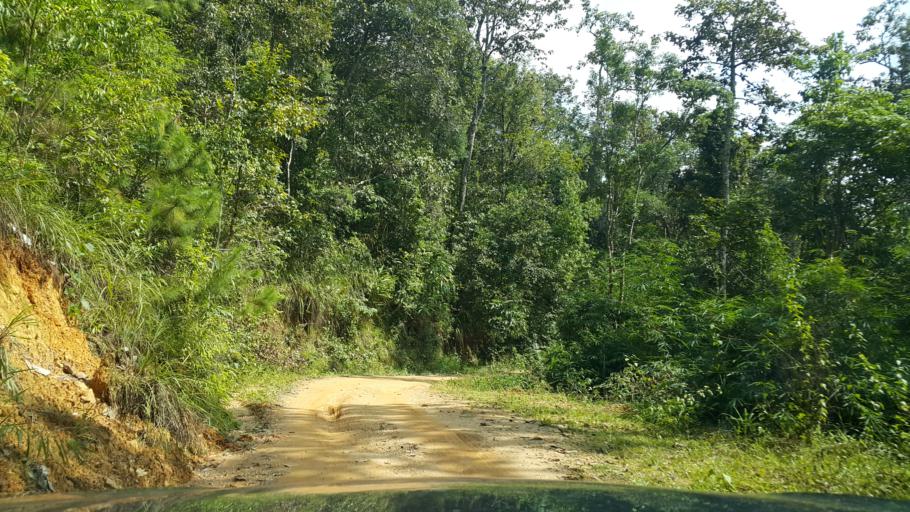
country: TH
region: Chiang Mai
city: Phrao
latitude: 19.1024
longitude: 99.2711
